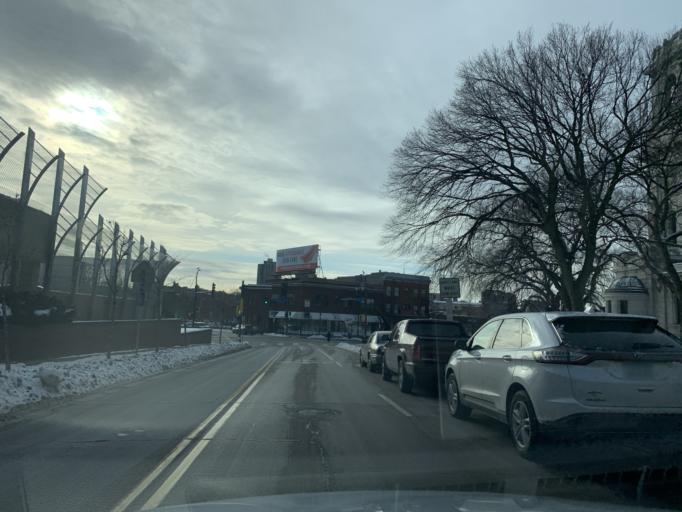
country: US
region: Minnesota
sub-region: Hennepin County
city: Minneapolis
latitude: 44.9733
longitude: -93.2856
